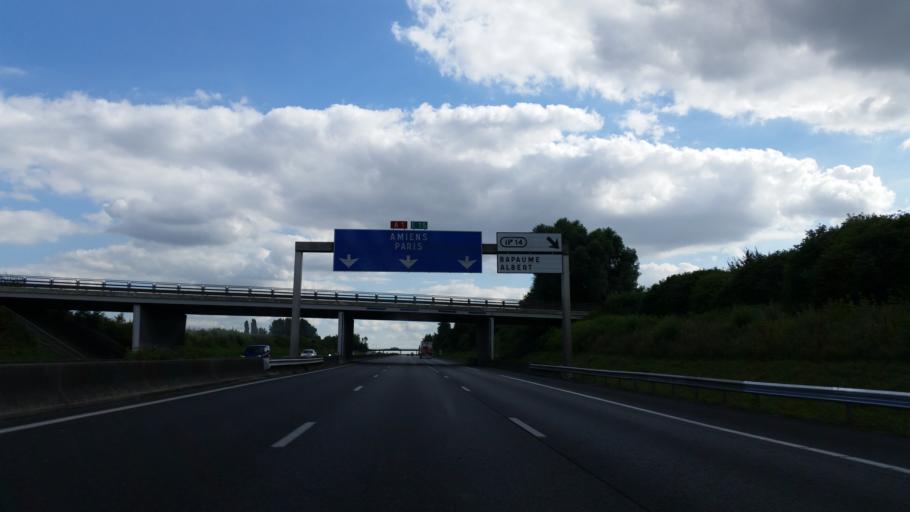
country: FR
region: Nord-Pas-de-Calais
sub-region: Departement du Pas-de-Calais
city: Bapaume
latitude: 50.1075
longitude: 2.8715
